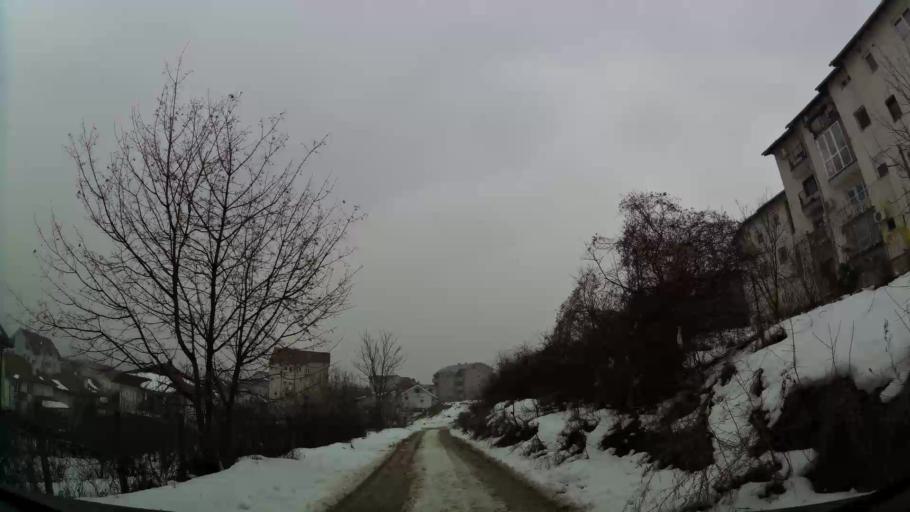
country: RS
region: Central Serbia
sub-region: Belgrade
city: Zvezdara
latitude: 44.7707
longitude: 20.5105
